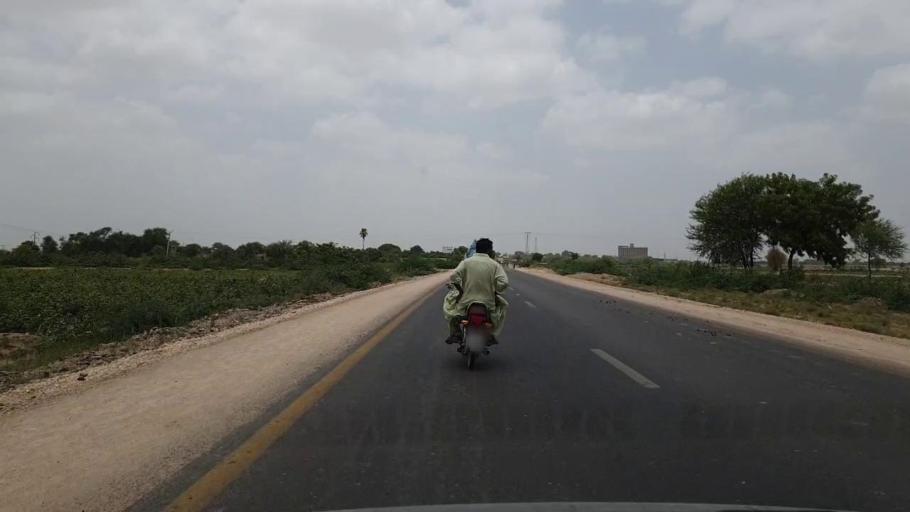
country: PK
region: Sindh
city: Naukot
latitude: 24.8434
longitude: 69.4286
